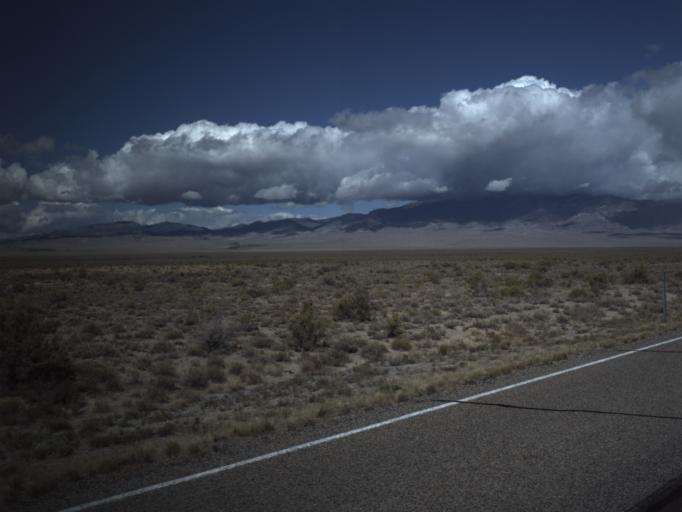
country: US
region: Nevada
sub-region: White Pine County
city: McGill
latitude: 39.0038
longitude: -114.0349
